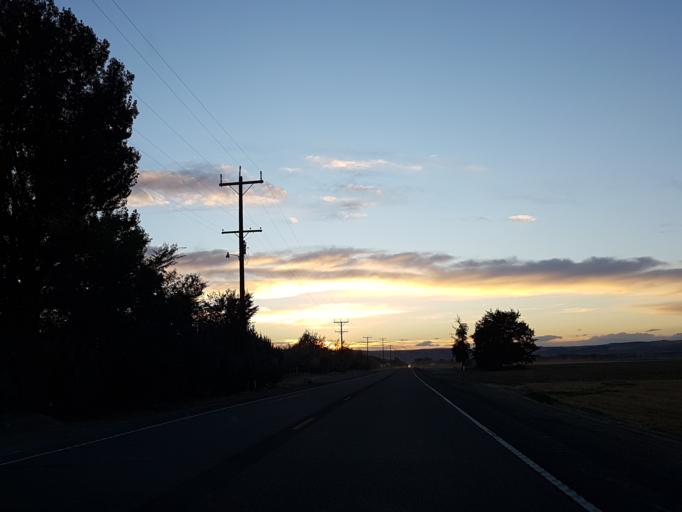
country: US
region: Oregon
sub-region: Malheur County
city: Vale
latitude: 43.9391
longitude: -117.3446
